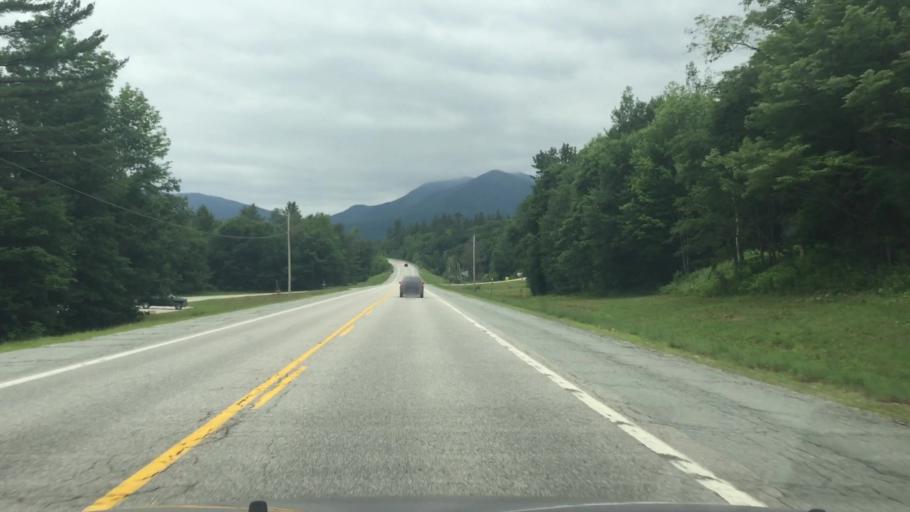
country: US
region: New Hampshire
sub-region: Carroll County
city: North Conway
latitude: 44.1193
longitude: -71.3542
